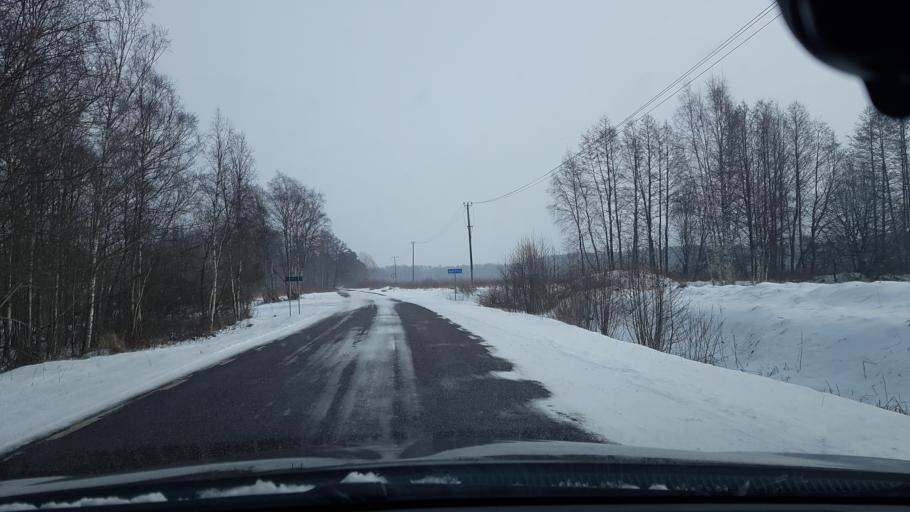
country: EE
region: Harju
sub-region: Kuusalu vald
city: Kuusalu
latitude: 59.4845
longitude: 25.3993
